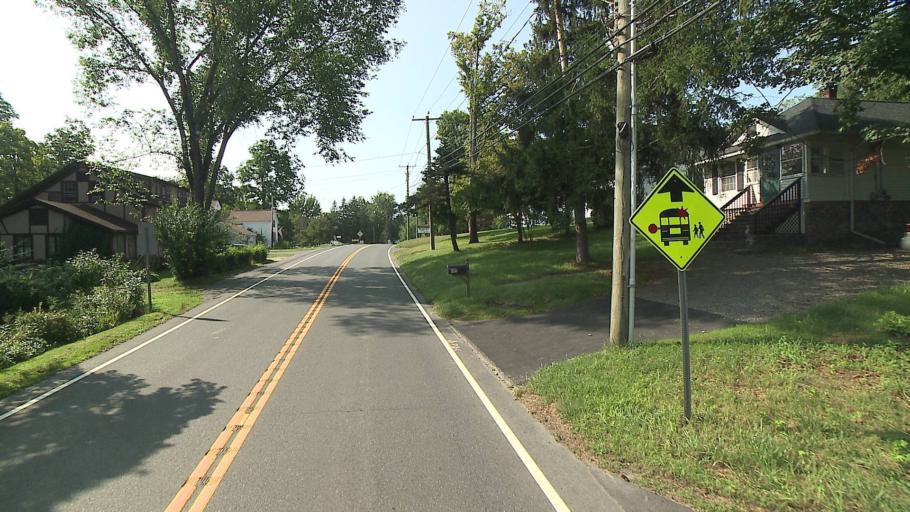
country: US
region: Connecticut
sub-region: Fairfield County
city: Sherman
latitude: 41.6451
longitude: -73.4841
